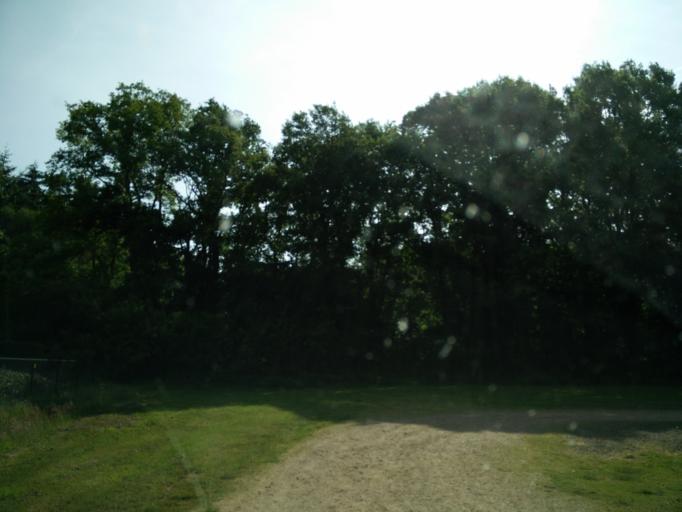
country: NL
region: Drenthe
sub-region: Gemeente Borger-Odoorn
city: Borger
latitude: 52.9556
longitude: 6.7887
